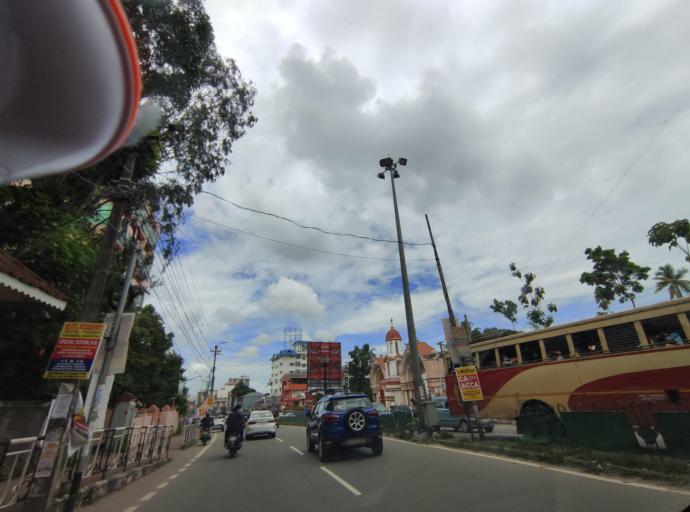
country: IN
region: Kerala
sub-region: Thiruvananthapuram
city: Thiruvananthapuram
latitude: 8.5264
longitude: 76.9391
